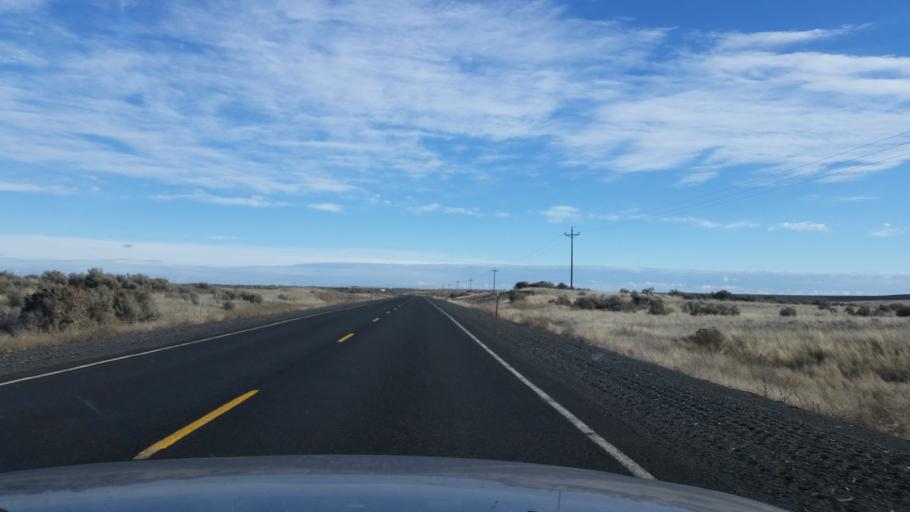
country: US
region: Washington
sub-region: Adams County
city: Ritzville
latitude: 47.3131
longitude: -118.7723
